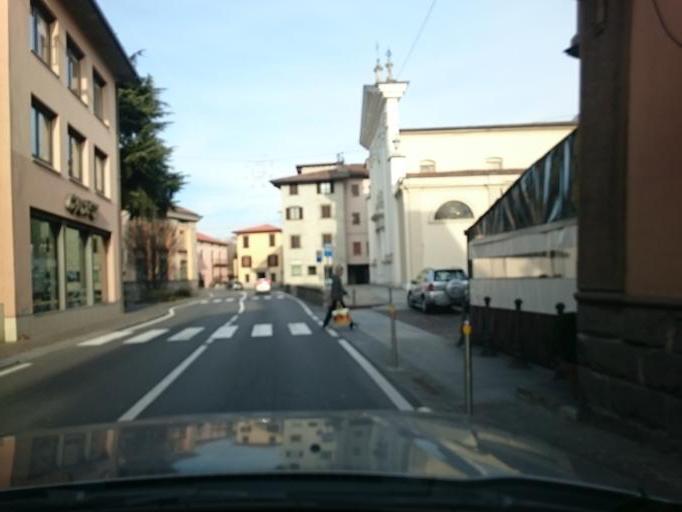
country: IT
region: Lombardy
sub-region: Provincia di Brescia
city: Darfo
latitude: 45.8798
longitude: 10.1821
